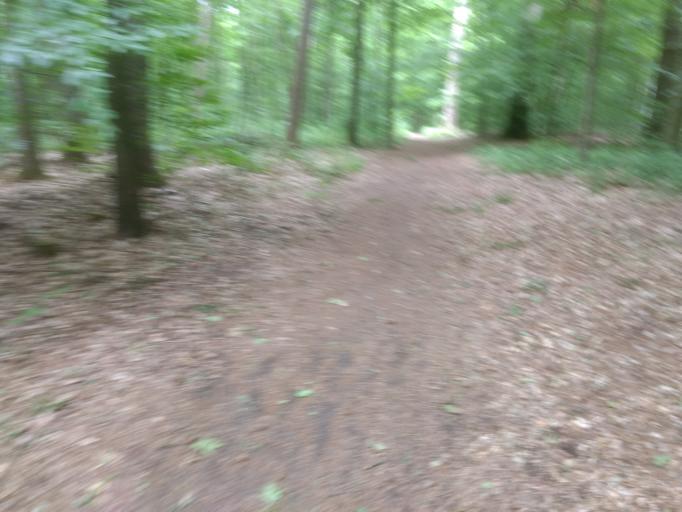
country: BE
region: Flanders
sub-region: Provincie Vlaams-Brabant
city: Oud-Heverlee
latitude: 50.8178
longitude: 4.6551
